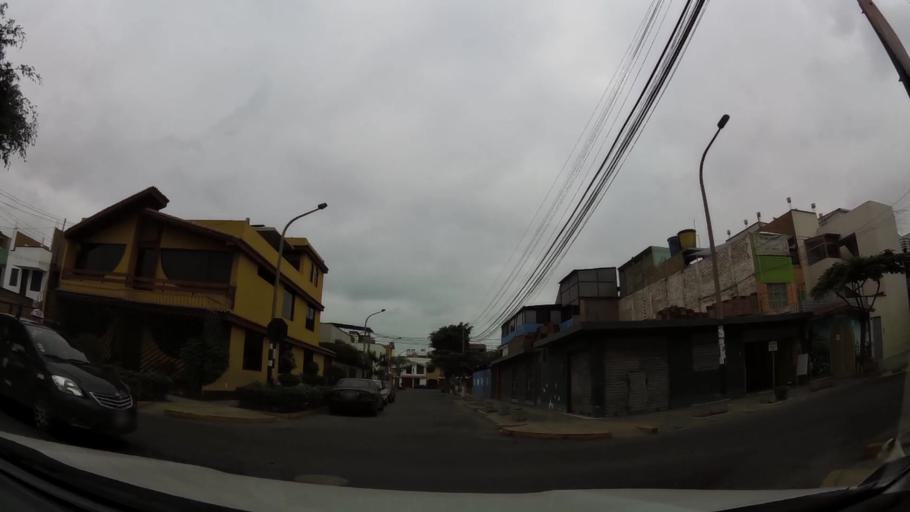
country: PE
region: Lima
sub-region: Lima
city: Surco
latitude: -12.1627
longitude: -76.9958
